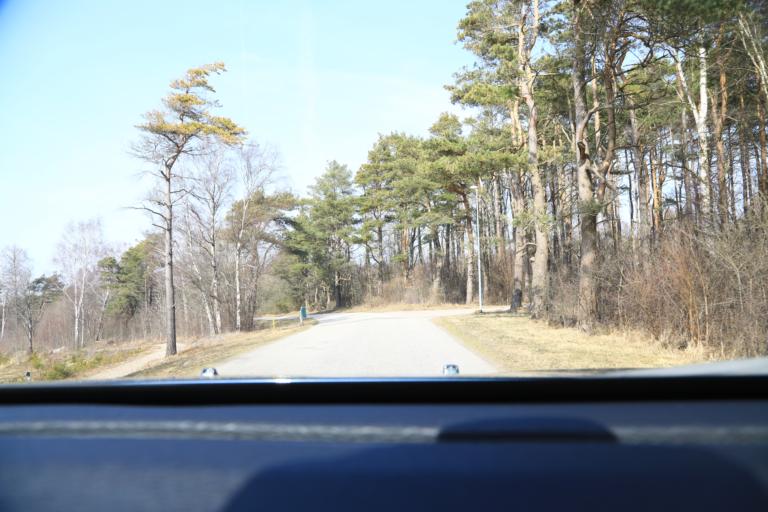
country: SE
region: Halland
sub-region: Kungsbacka Kommun
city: Frillesas
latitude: 57.2595
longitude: 12.1245
